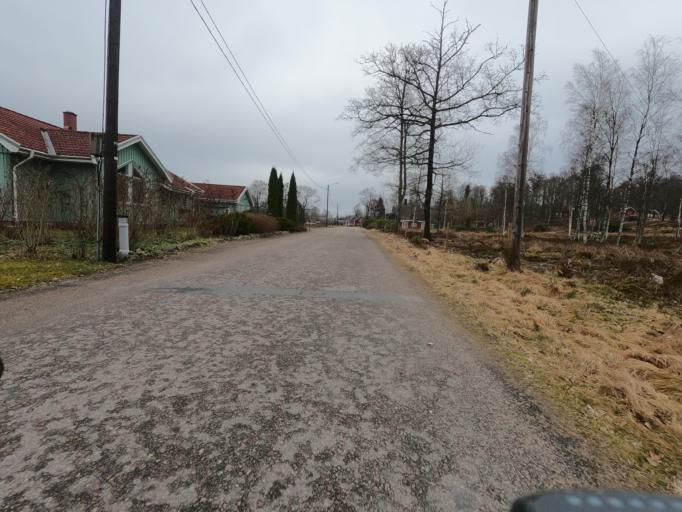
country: SE
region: Kronoberg
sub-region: Ljungby Kommun
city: Ljungby
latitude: 56.8138
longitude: 13.6944
